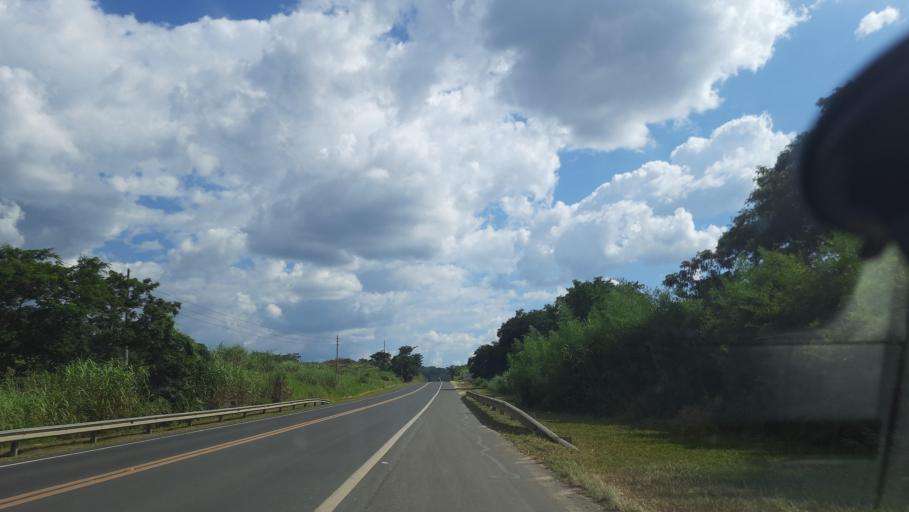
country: BR
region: Sao Paulo
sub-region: Sao Jose Do Rio Pardo
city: Sao Jose do Rio Pardo
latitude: -21.6385
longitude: -46.9052
